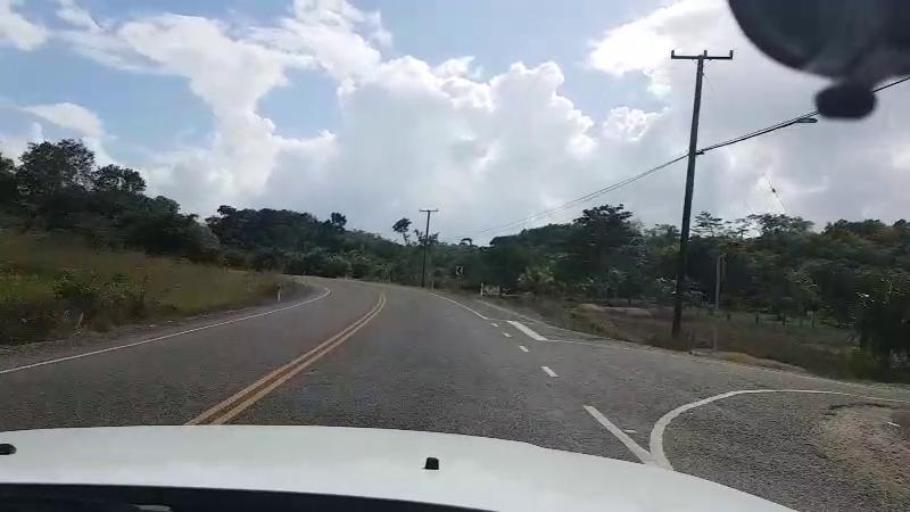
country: BZ
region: Cayo
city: Belmopan
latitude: 17.2280
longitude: -88.7794
